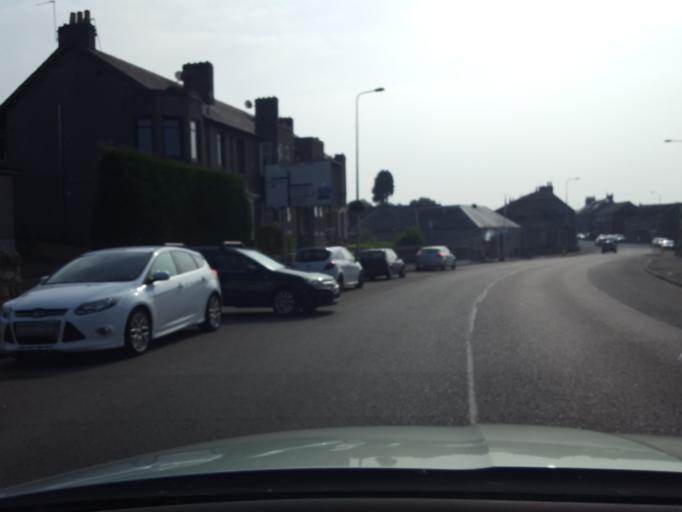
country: GB
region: Scotland
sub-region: Fife
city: Crossgates
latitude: 56.0862
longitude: -3.3738
